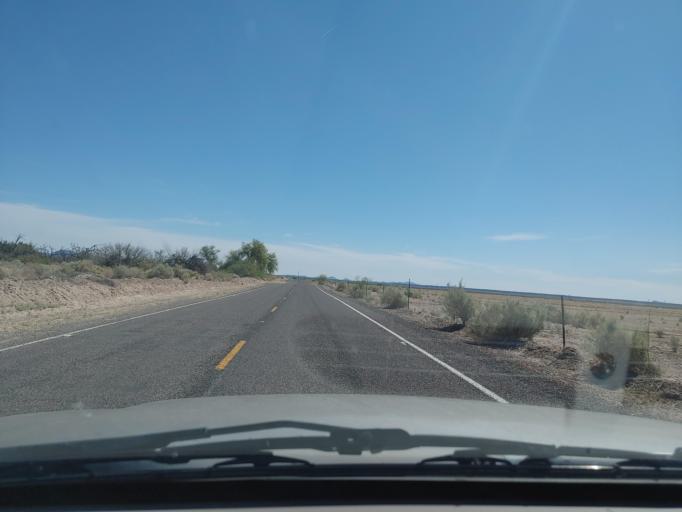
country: US
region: Arizona
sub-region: Maricopa County
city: Gila Bend
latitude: 32.9864
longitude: -113.3122
